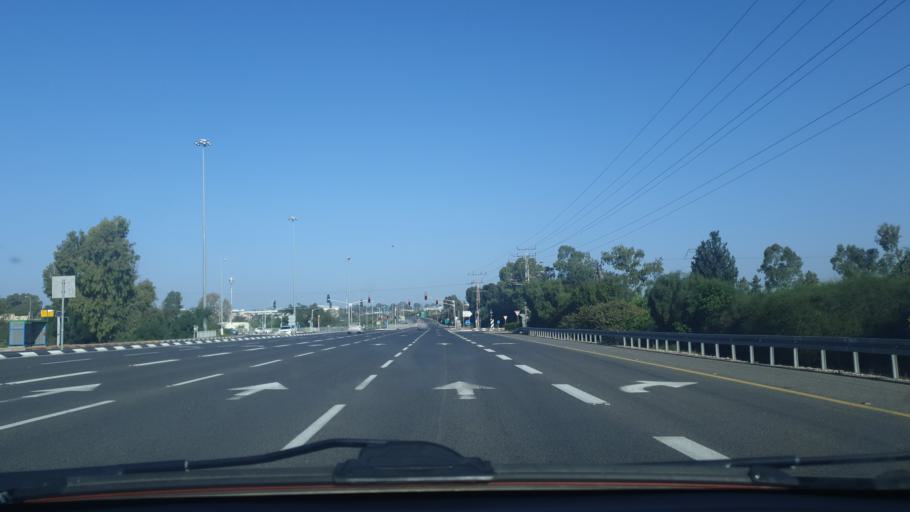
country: IL
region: Central District
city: Ramla
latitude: 31.9502
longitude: 34.8573
